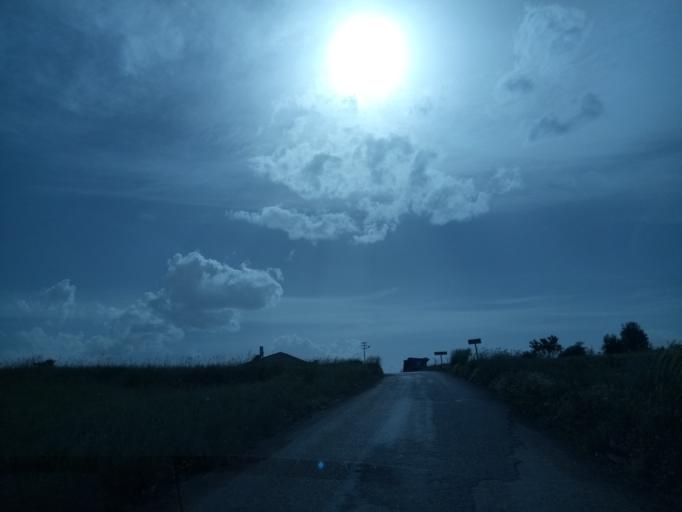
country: TR
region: Konya
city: Ahirli
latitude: 37.2843
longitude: 32.1846
